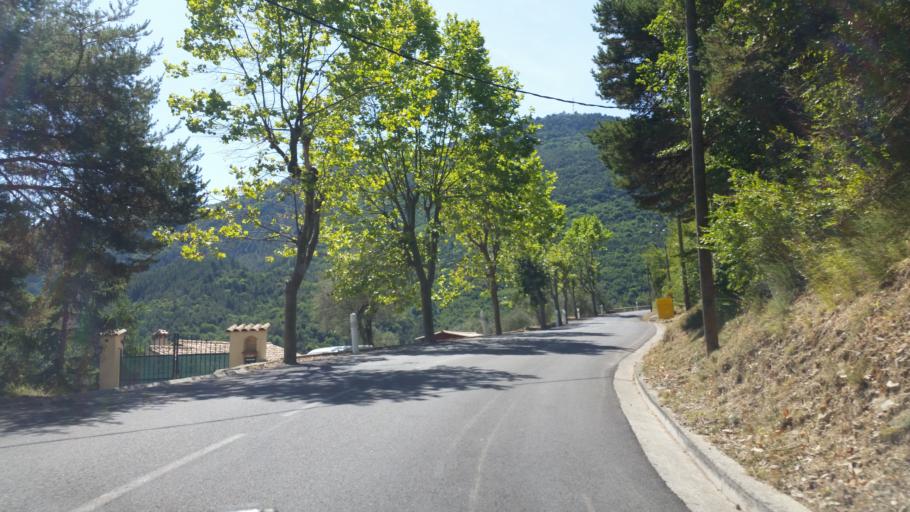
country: FR
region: Provence-Alpes-Cote d'Azur
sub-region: Departement des Alpes-Maritimes
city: Breil-sur-Roya
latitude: 43.9413
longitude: 7.4923
